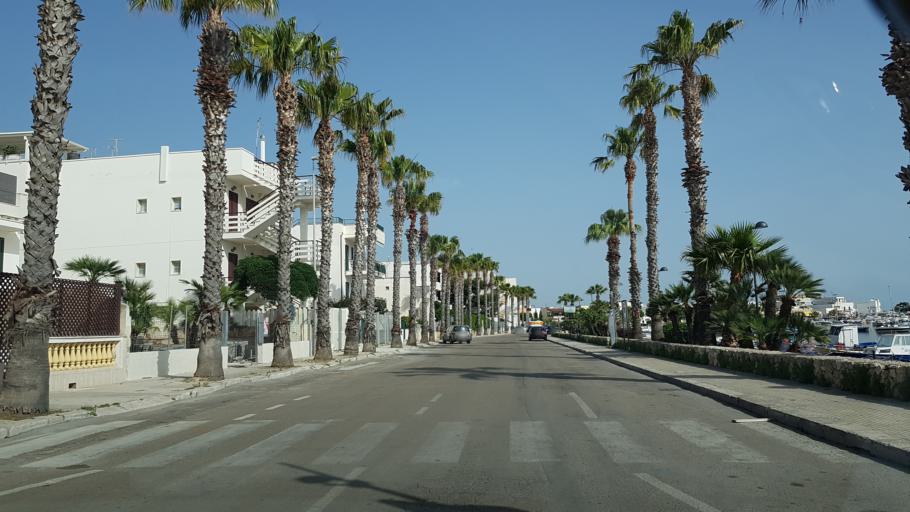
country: IT
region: Apulia
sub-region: Provincia di Lecce
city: Porto Cesareo
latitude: 40.2616
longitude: 17.8894
